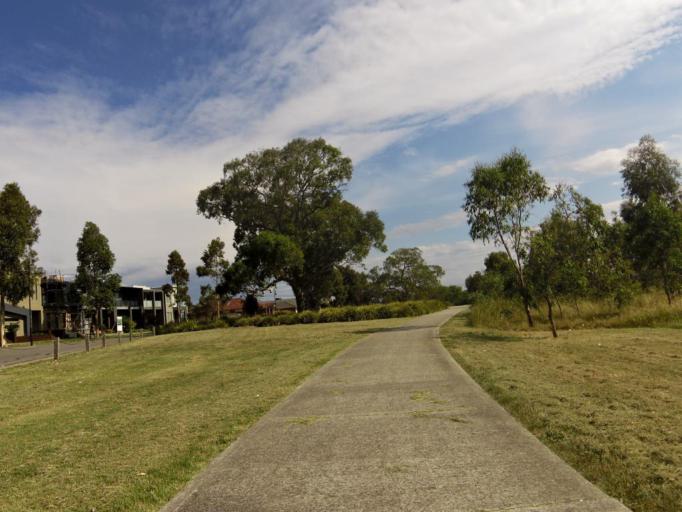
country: AU
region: Victoria
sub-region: Whittlesea
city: Epping
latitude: -37.6310
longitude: 145.0333
